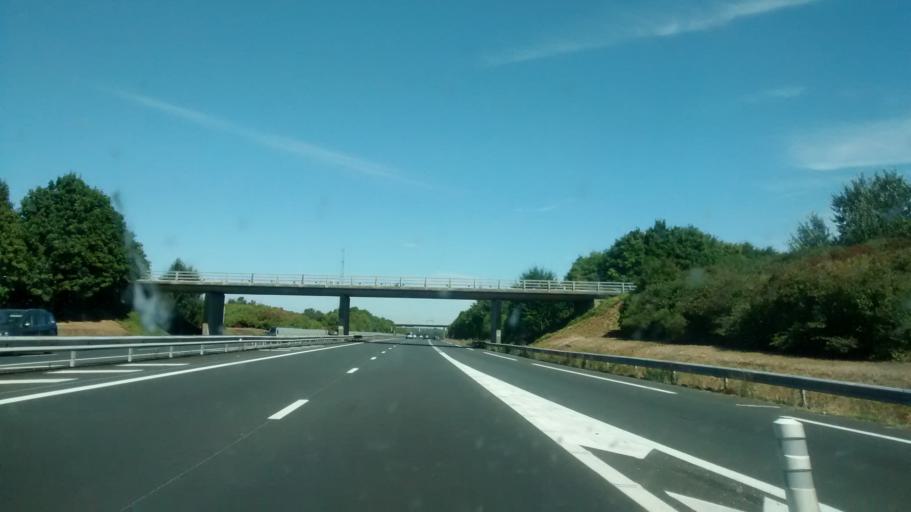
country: FR
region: Poitou-Charentes
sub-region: Departement des Deux-Sevres
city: Fors
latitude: 46.2375
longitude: -0.4366
